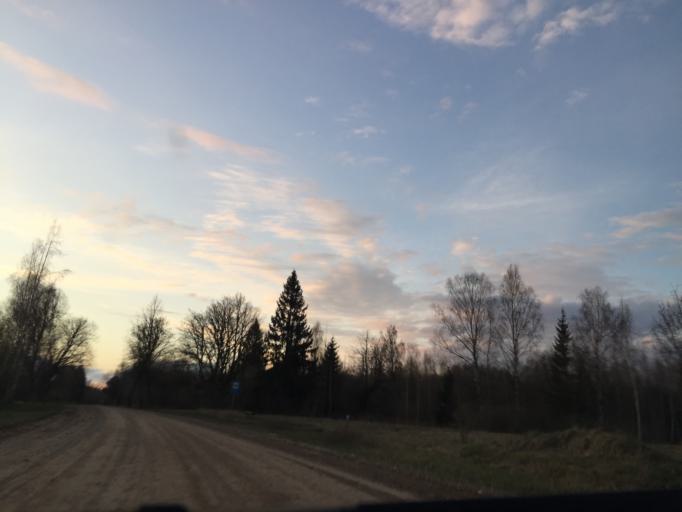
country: LV
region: Aluksnes Rajons
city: Aluksne
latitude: 57.2961
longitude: 26.9190
